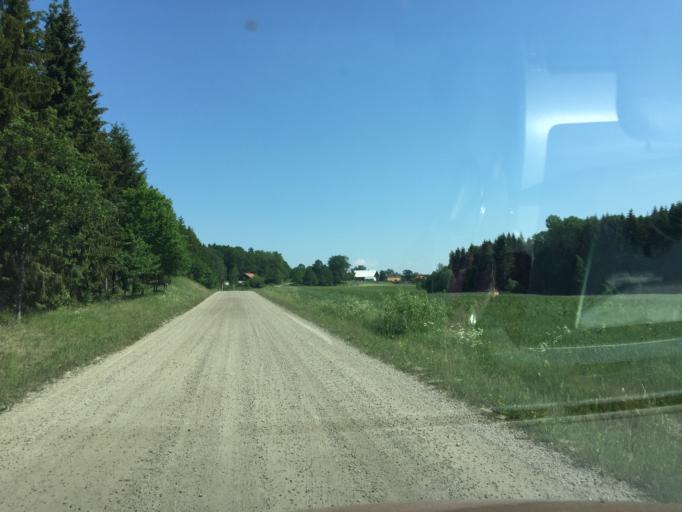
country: SE
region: Soedermanland
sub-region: Flens Kommun
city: Flen
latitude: 58.9290
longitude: 16.4570
